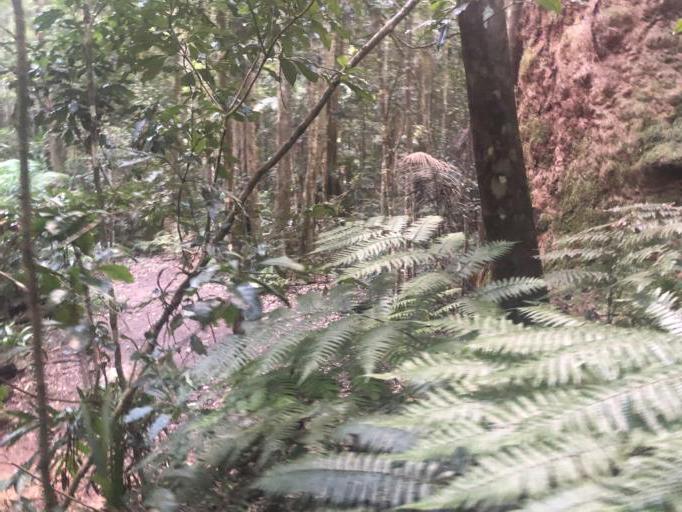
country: AU
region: New South Wales
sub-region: Coffs Harbour
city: Coffs Harbour
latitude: -30.2417
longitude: 153.0958
